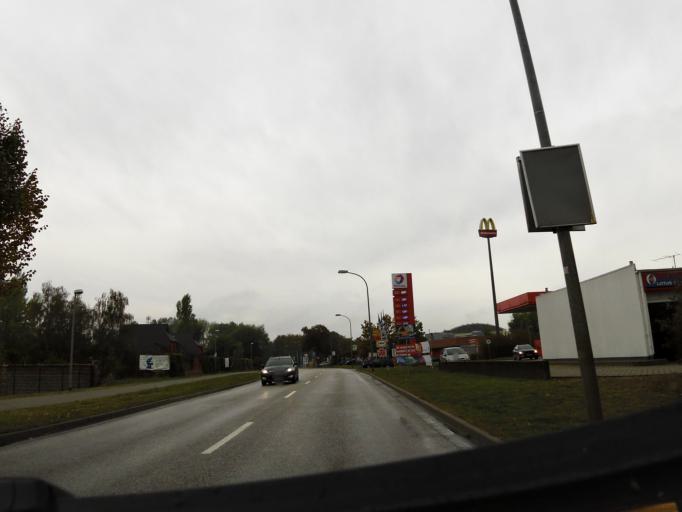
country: DE
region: Saxony-Anhalt
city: Koethen
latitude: 51.7653
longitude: 11.9884
